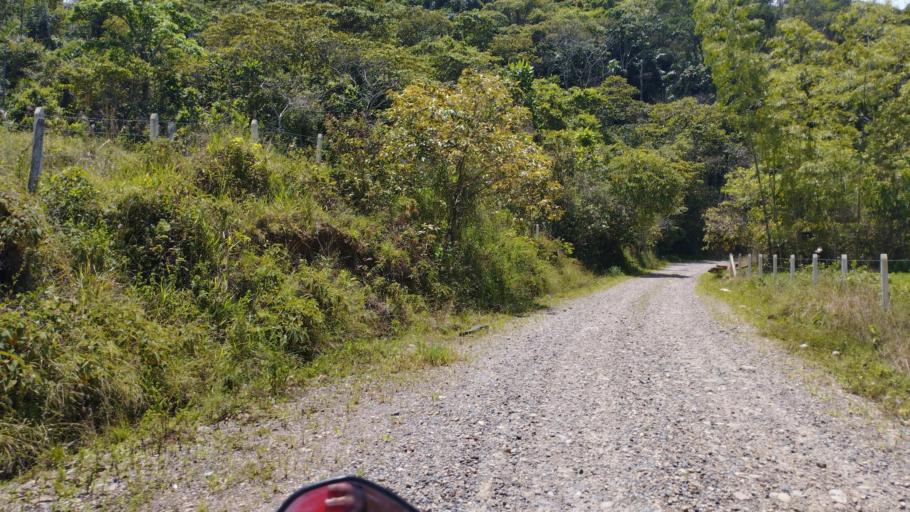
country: CO
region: Boyaca
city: San Luis de Gaceno
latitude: 4.7494
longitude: -73.1426
